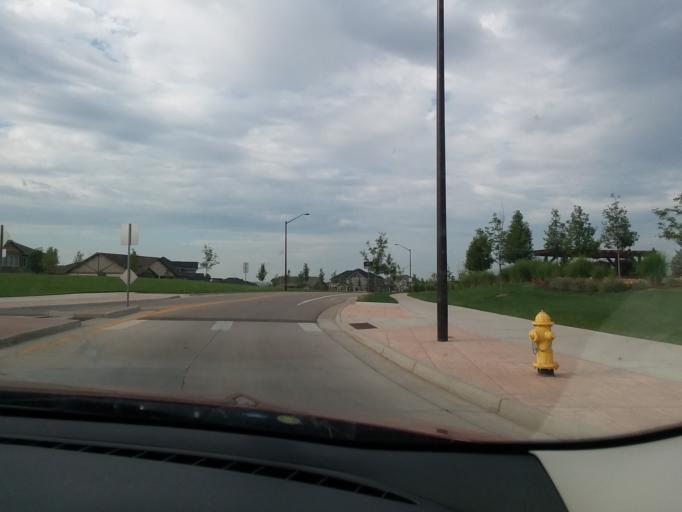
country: US
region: Colorado
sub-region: Larimer County
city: Fort Collins
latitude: 40.5015
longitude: -105.0241
